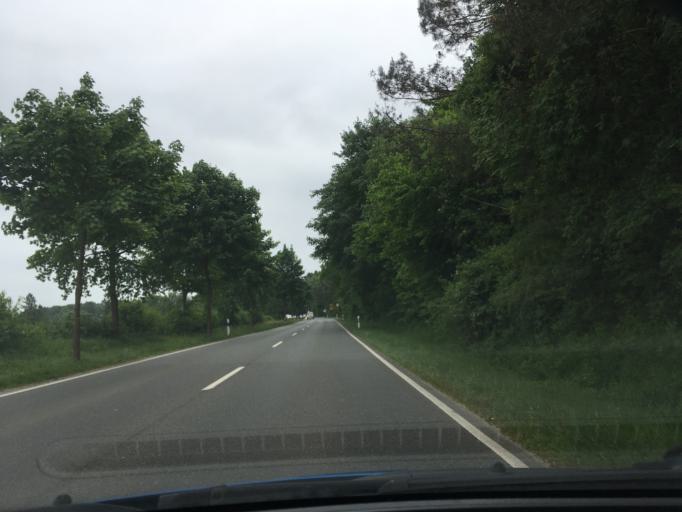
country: DE
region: Lower Saxony
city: Buchholz in der Nordheide
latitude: 53.3462
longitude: 9.8773
